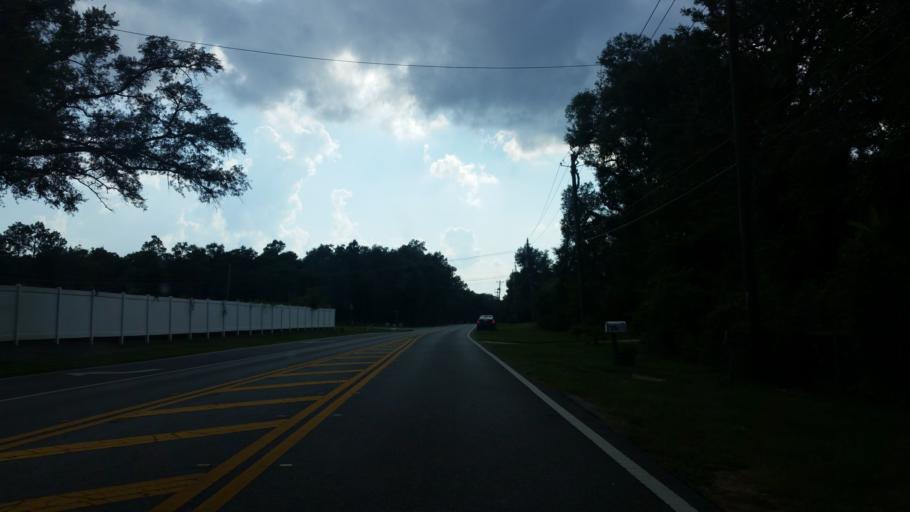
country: US
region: Florida
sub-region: Santa Rosa County
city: Bagdad
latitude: 30.6005
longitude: -87.0425
